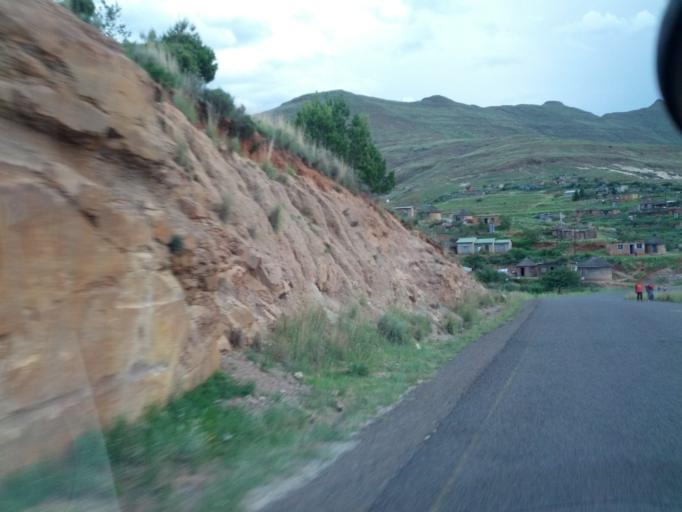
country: LS
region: Qacha's Nek
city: Qacha's Nek
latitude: -30.0763
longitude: 28.5822
